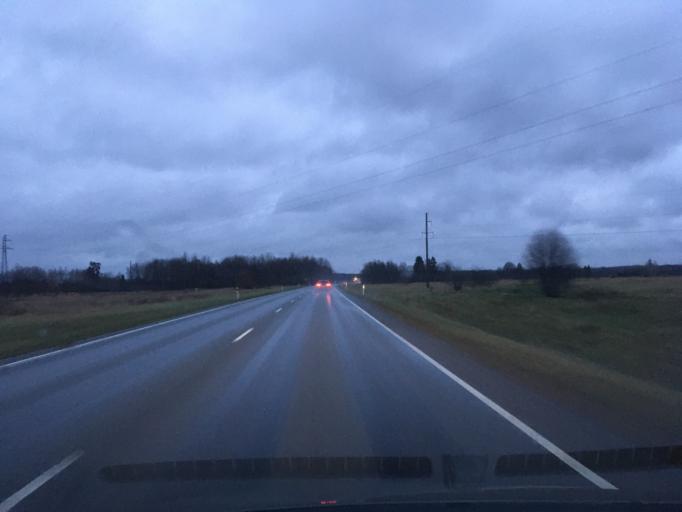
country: EE
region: Laeaene
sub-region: Lihula vald
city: Lihula
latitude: 58.7015
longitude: 23.8359
